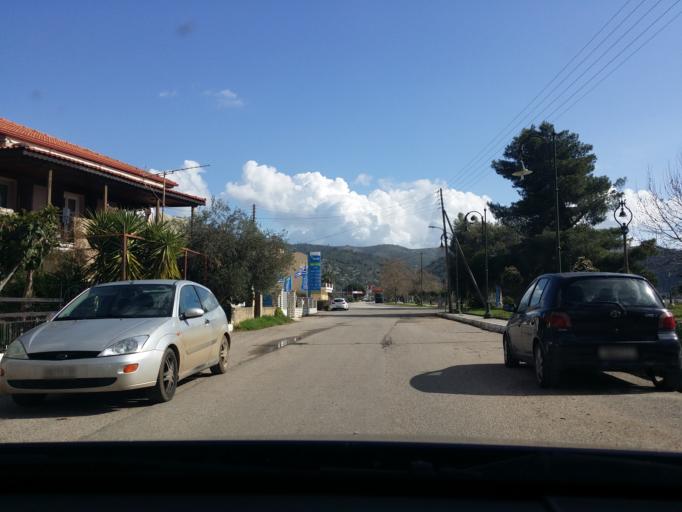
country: GR
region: West Greece
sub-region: Nomos Aitolias kai Akarnanias
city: Astakos
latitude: 38.5357
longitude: 21.0872
